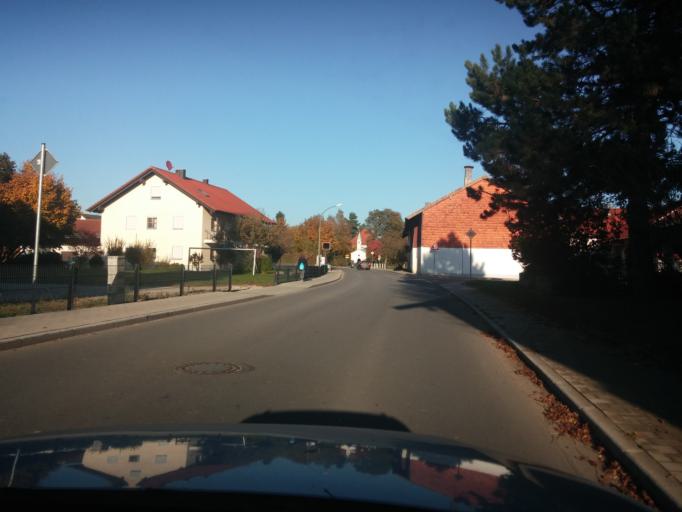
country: DE
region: Bavaria
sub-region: Upper Bavaria
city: Pastetten
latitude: 48.1998
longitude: 11.9456
